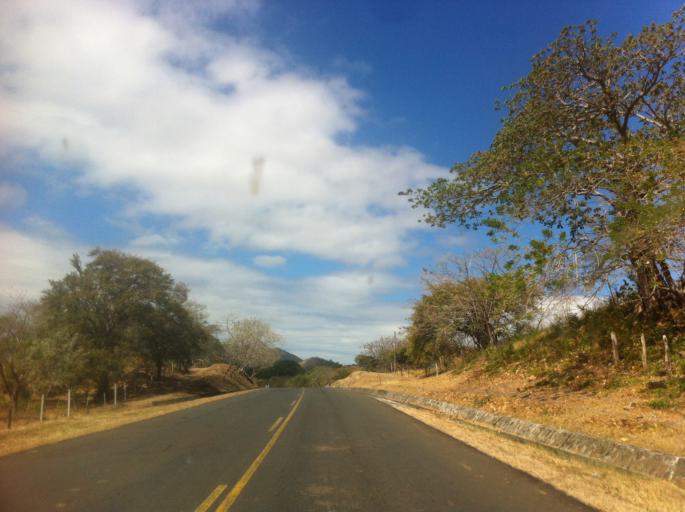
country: NI
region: Chontales
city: Acoyapa
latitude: 12.0039
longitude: -85.1774
